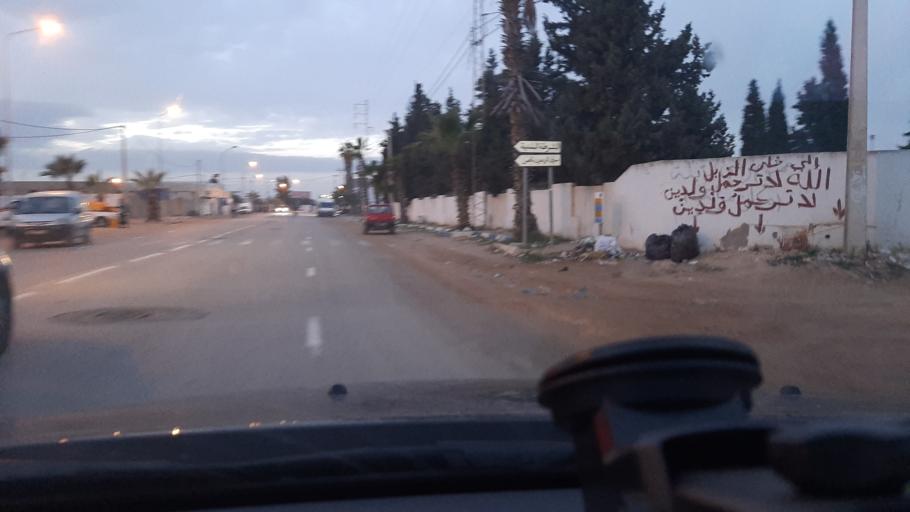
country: TN
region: Safaqis
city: Sfax
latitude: 34.7705
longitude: 10.6807
